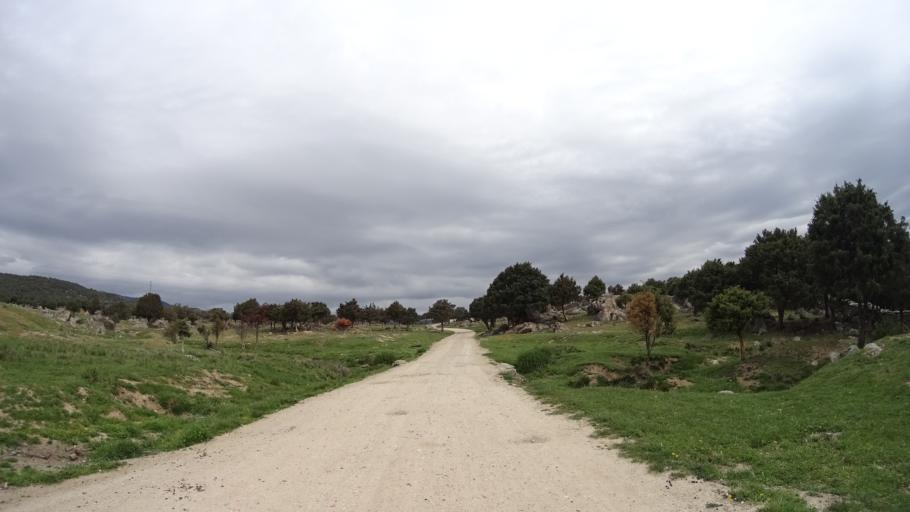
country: ES
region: Madrid
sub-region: Provincia de Madrid
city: Hoyo de Manzanares
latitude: 40.6046
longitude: -3.8780
